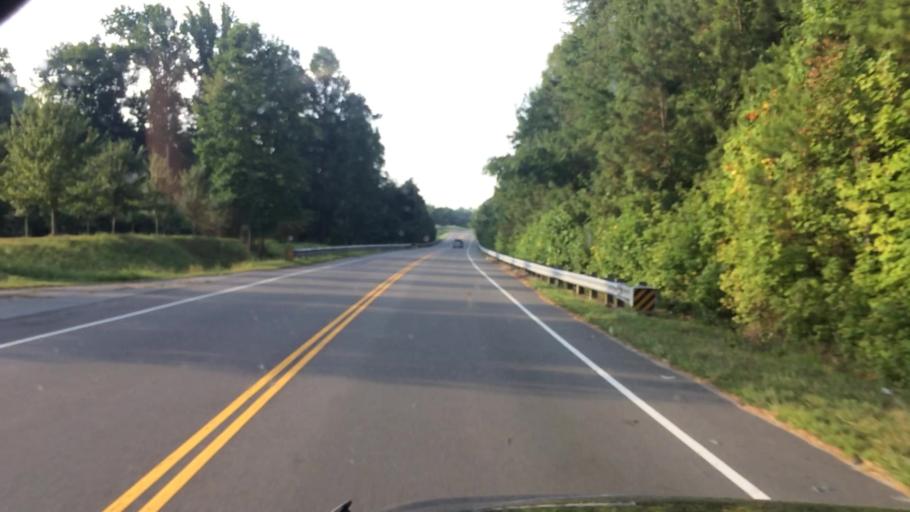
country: US
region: Virginia
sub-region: James City County
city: Williamsburg
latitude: 37.2997
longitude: -76.7256
